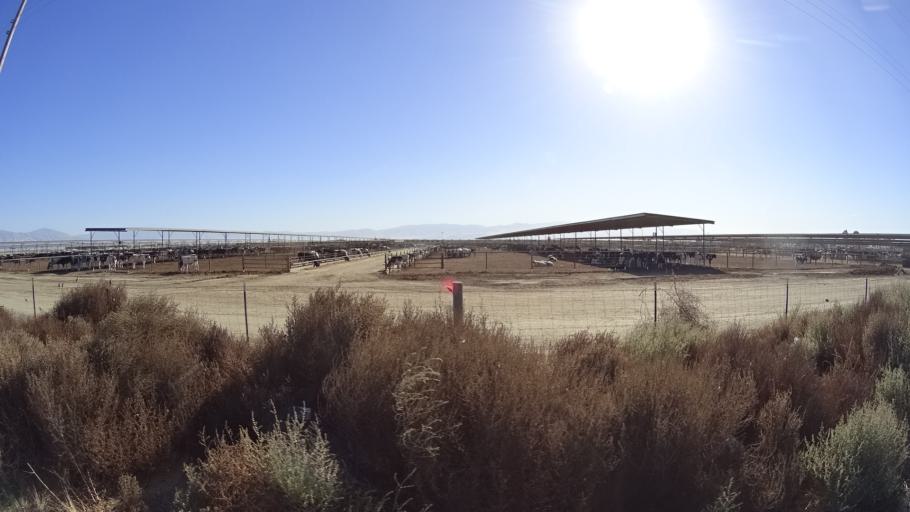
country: US
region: California
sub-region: Kern County
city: Greenfield
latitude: 35.2814
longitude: -118.9898
